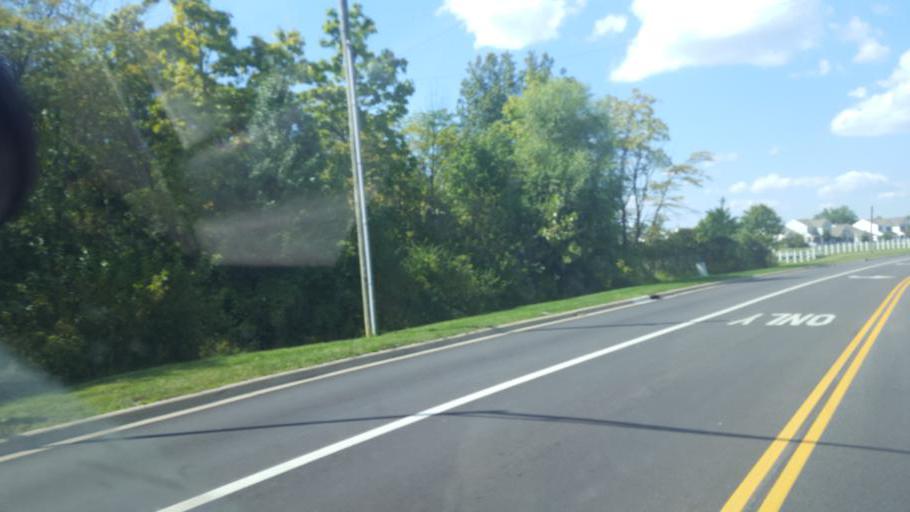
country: US
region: Ohio
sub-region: Franklin County
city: Grove City
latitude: 39.8986
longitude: -83.1076
